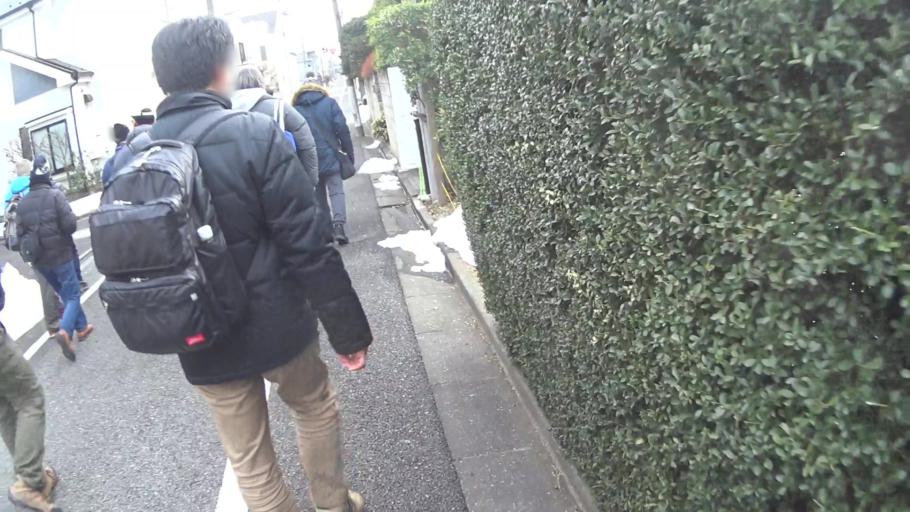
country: JP
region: Tokyo
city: Musashino
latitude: 35.7209
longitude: 139.6046
